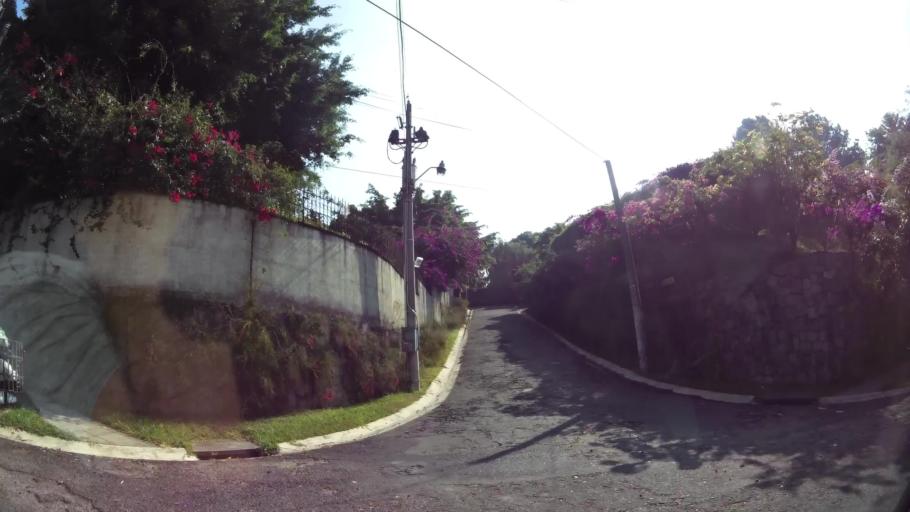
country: SV
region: La Libertad
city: Antiguo Cuscatlan
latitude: 13.6782
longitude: -89.2312
